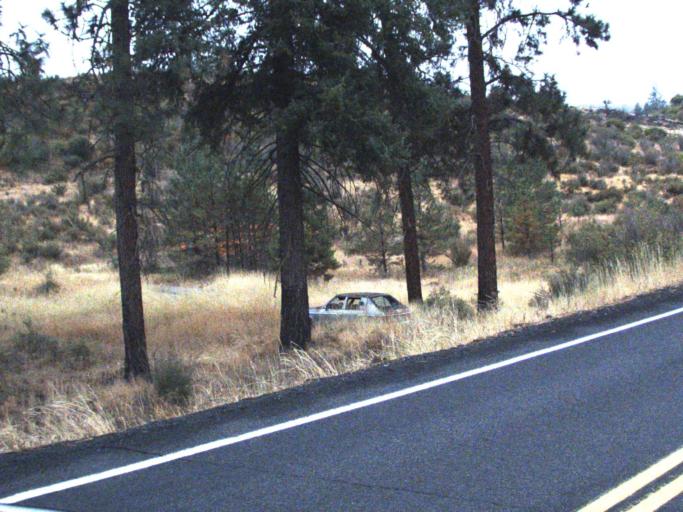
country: US
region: Washington
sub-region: Spokane County
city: Fairchild Air Force Base
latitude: 47.7791
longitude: -117.8886
